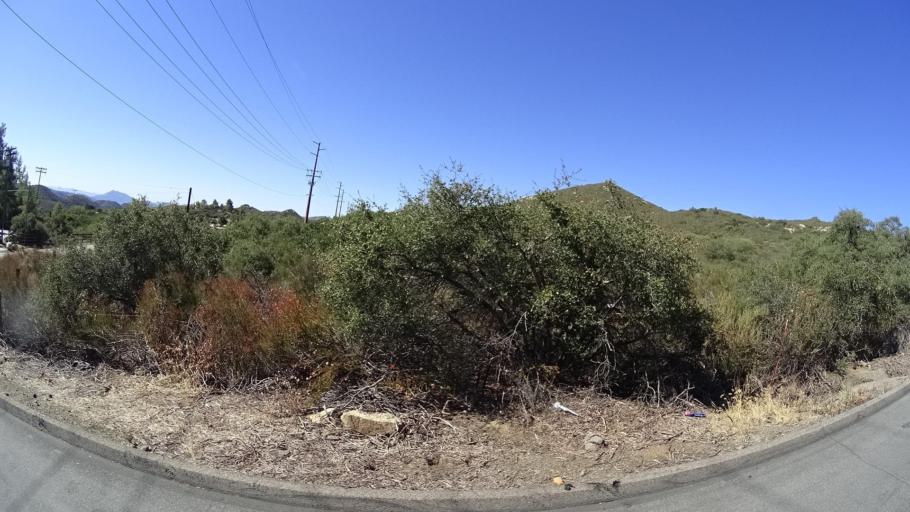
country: US
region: California
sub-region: San Diego County
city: Descanso
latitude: 32.8068
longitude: -116.6391
